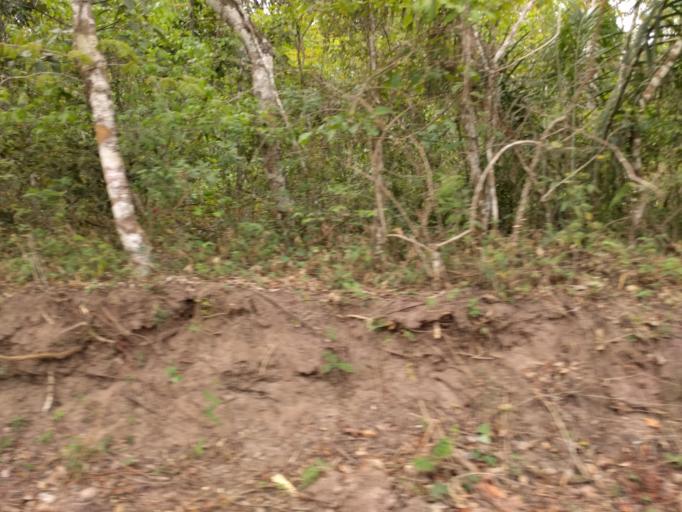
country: BO
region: Santa Cruz
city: Santiago del Torno
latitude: -17.9085
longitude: -63.4377
